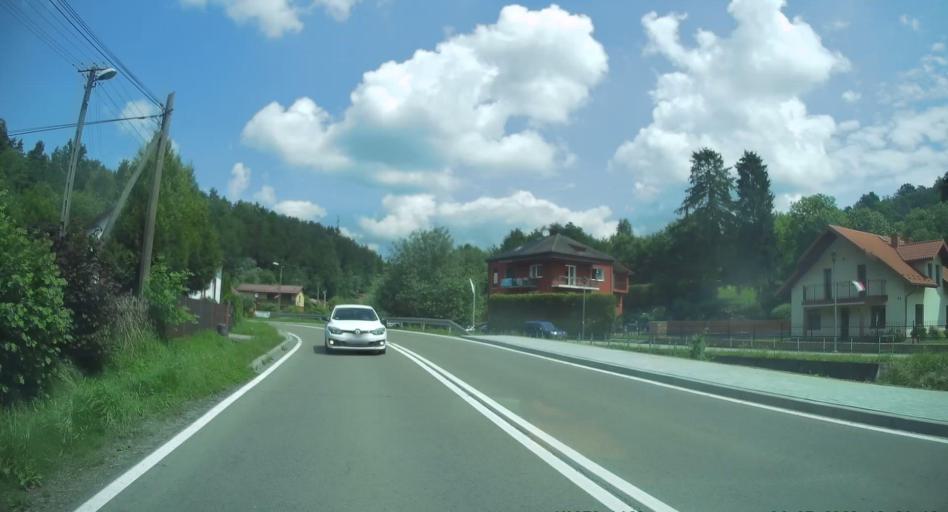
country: PL
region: Lesser Poland Voivodeship
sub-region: Powiat nowosadecki
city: Nowy Sacz
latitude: 49.6404
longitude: 20.7152
